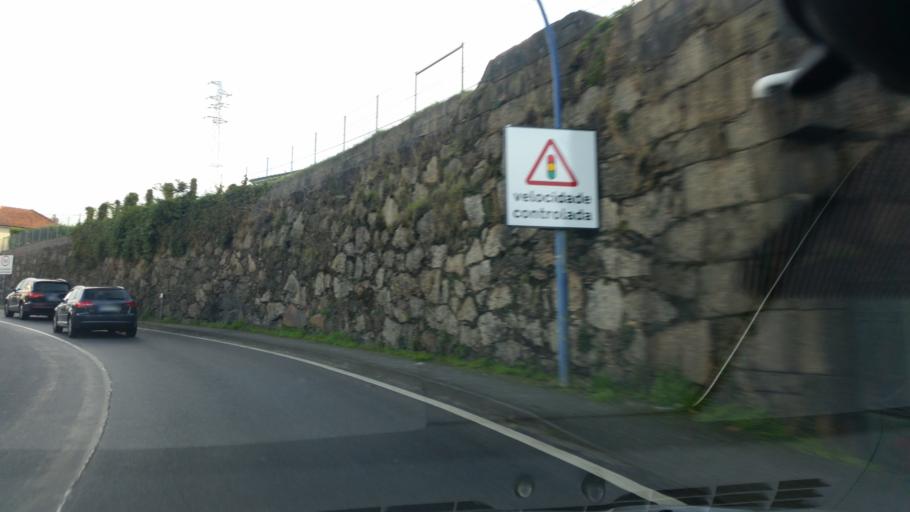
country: PT
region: Porto
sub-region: Santo Tirso
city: Sao Miguel do Couto
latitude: 41.3559
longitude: -8.4465
